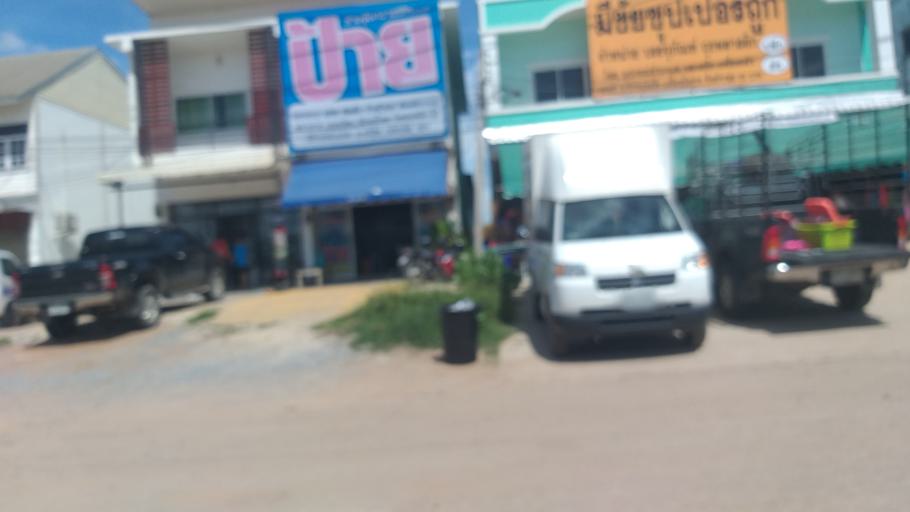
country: TH
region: Khon Kaen
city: Nong Ruea
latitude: 16.4904
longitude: 102.4350
